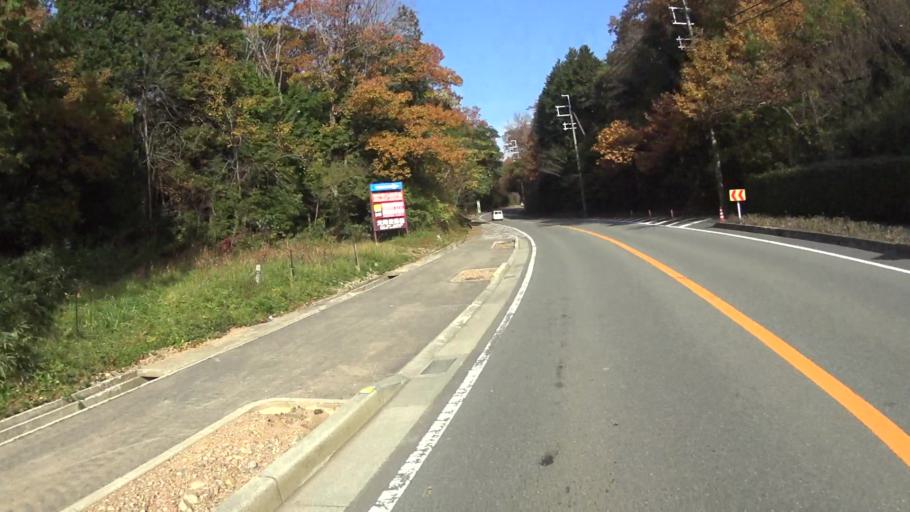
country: JP
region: Kyoto
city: Fukuchiyama
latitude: 35.2587
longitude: 135.1463
